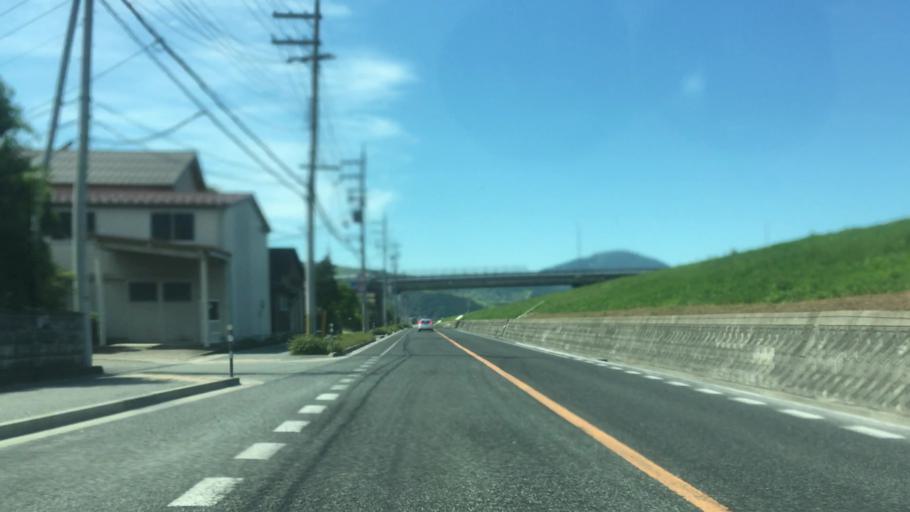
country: JP
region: Hyogo
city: Toyooka
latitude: 35.5541
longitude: 134.8204
